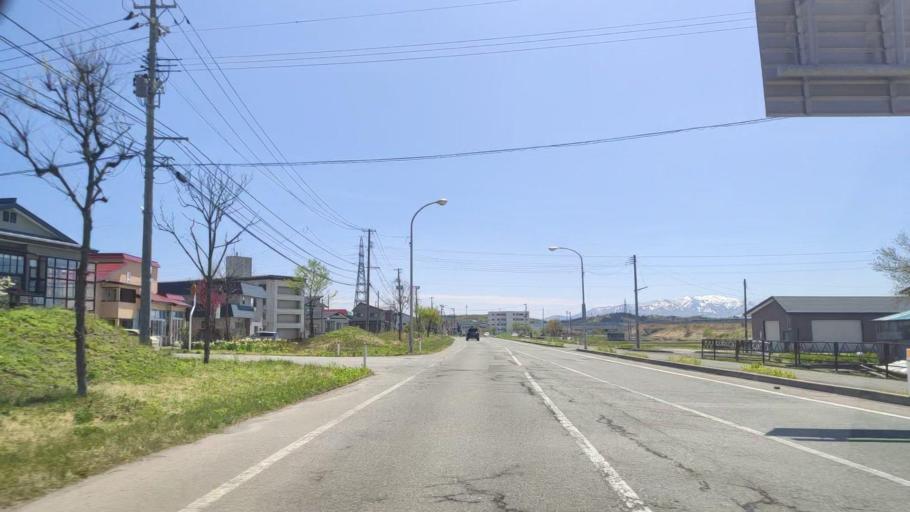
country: JP
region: Yamagata
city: Shinjo
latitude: 38.7493
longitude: 140.2955
